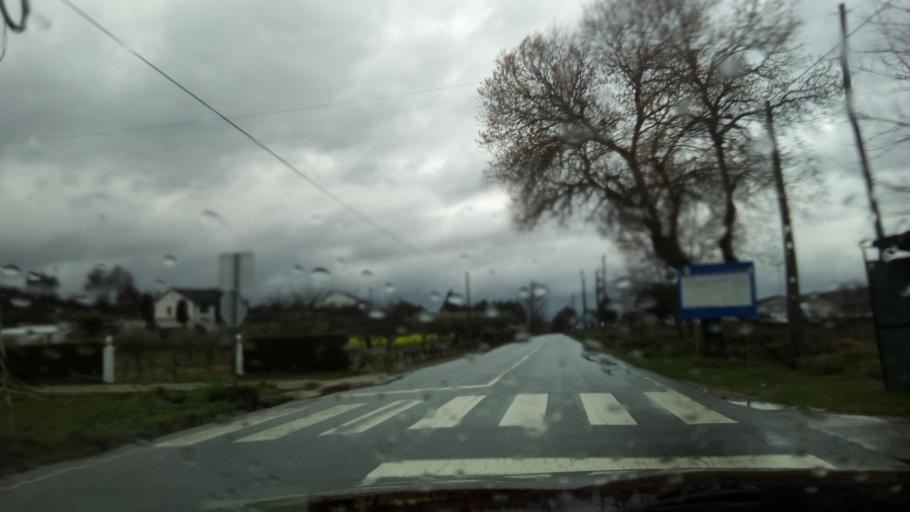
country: PT
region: Guarda
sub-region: Celorico da Beira
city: Celorico da Beira
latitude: 40.6151
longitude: -7.3069
